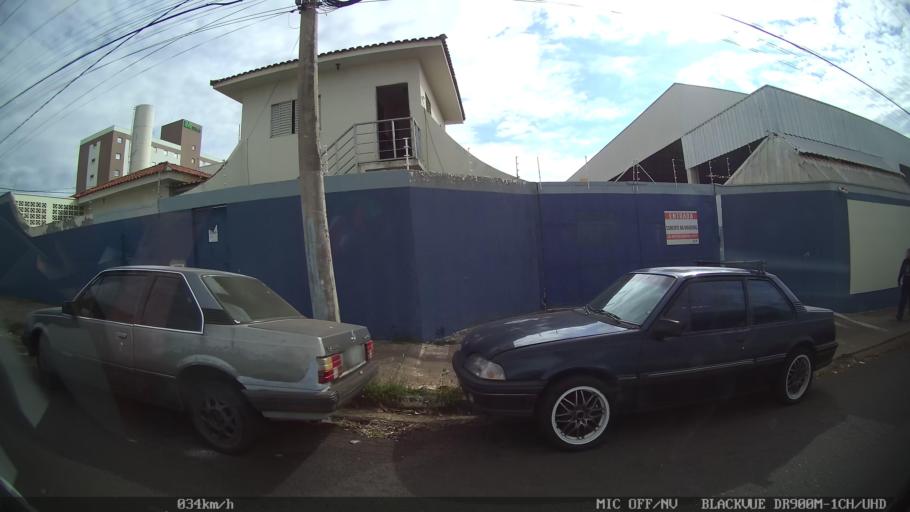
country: BR
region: Sao Paulo
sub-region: Sao Jose Do Rio Preto
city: Sao Jose do Rio Preto
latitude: -20.8265
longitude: -49.4055
